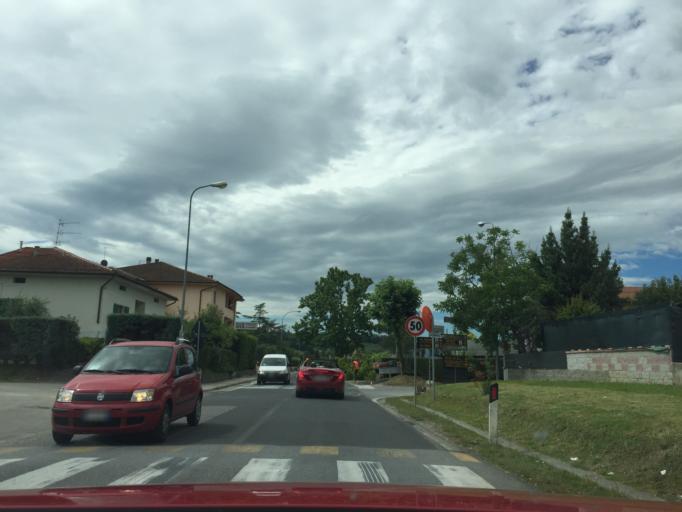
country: IT
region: Tuscany
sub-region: Province of Florence
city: Fucecchio
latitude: 43.7453
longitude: 10.8191
